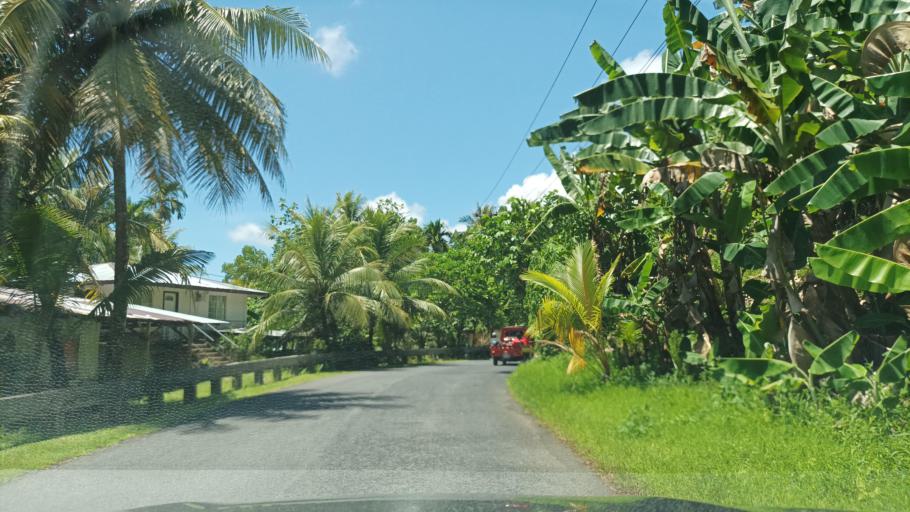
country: FM
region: Pohnpei
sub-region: Kolonia Municipality
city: Kolonia
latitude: 6.9581
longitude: 158.2785
